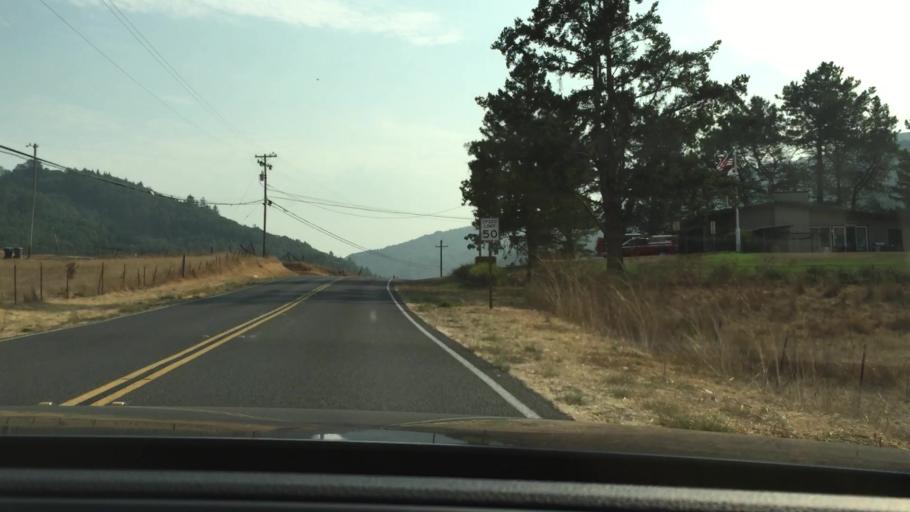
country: US
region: California
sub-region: Sonoma County
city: Petaluma
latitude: 38.1390
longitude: -122.7074
